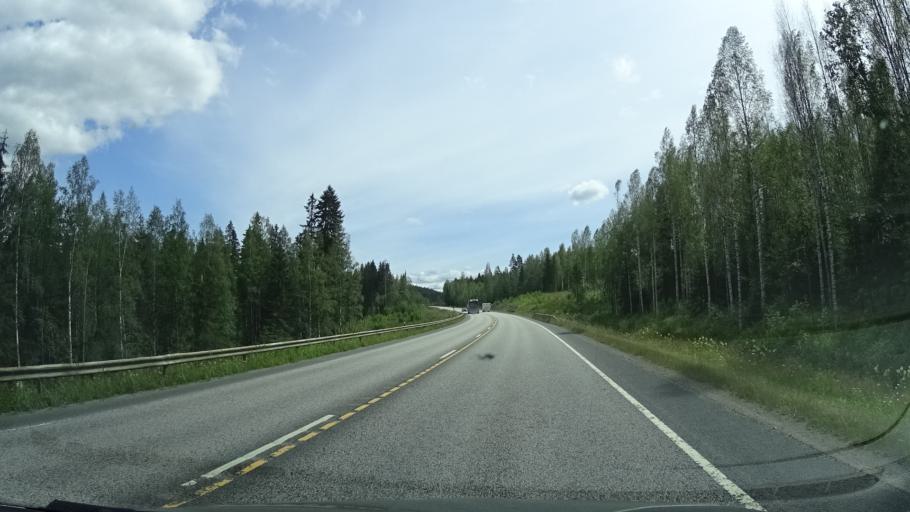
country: FI
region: Central Finland
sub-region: Jyvaeskylae
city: Jyvaeskylae
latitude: 62.2545
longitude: 25.6271
